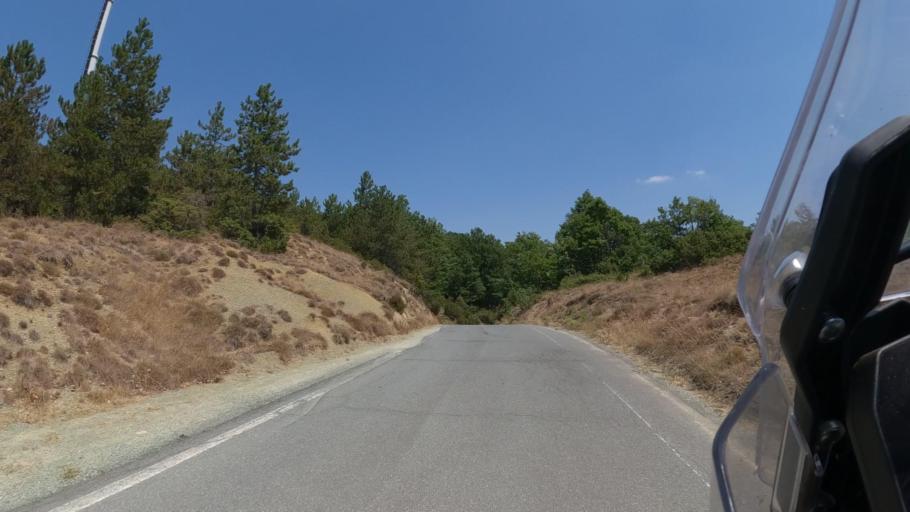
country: IT
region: Piedmont
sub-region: Provincia di Alessandria
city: Morbello
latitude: 44.5750
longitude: 8.5275
